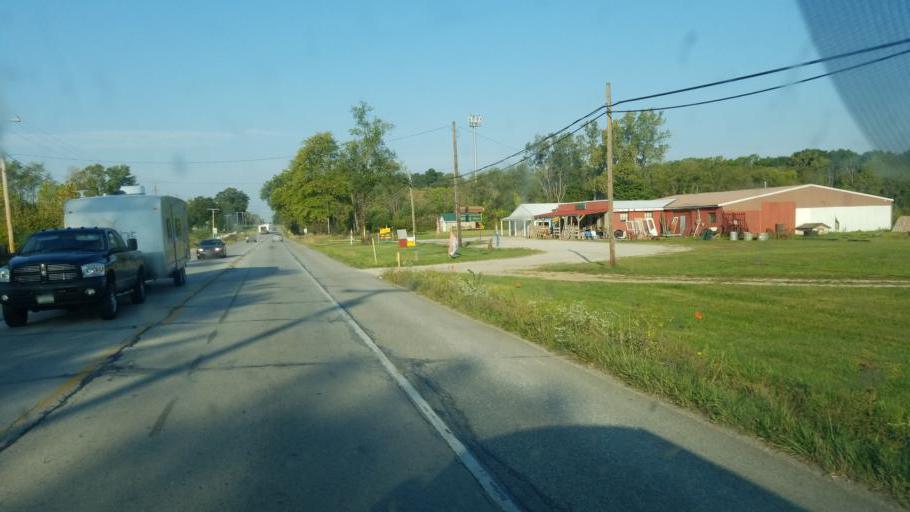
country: US
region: Indiana
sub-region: LaGrange County
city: Lagrange
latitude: 41.6415
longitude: -85.4293
